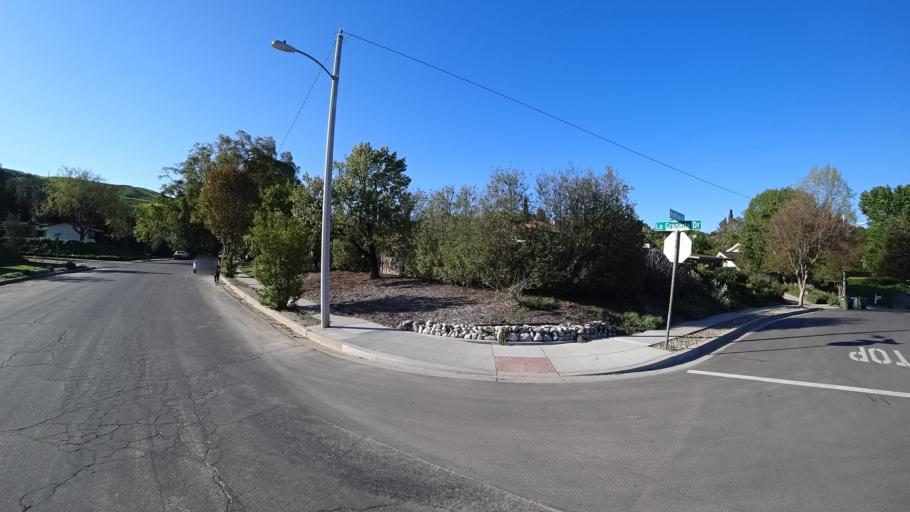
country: US
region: California
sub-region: Ventura County
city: Thousand Oaks
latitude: 34.1900
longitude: -118.8382
